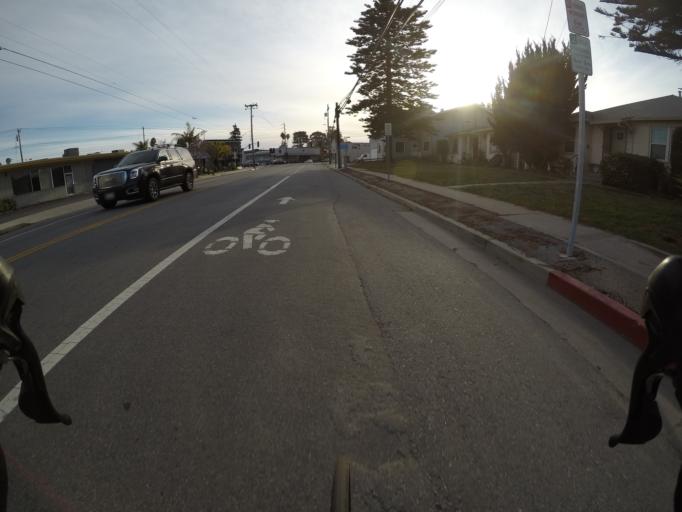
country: US
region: California
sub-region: Santa Cruz County
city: Santa Cruz
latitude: 36.9778
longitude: -122.0157
